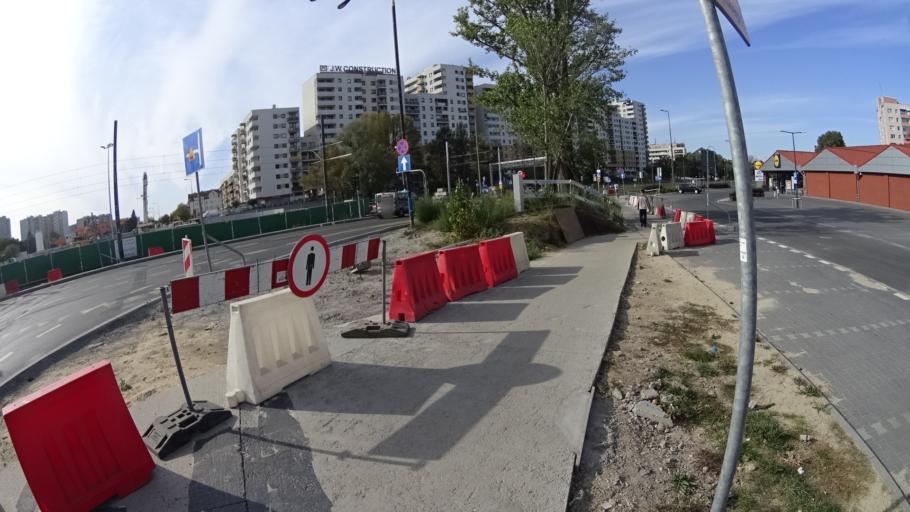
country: PL
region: Masovian Voivodeship
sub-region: Warszawa
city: Bemowo
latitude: 52.2396
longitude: 20.9140
